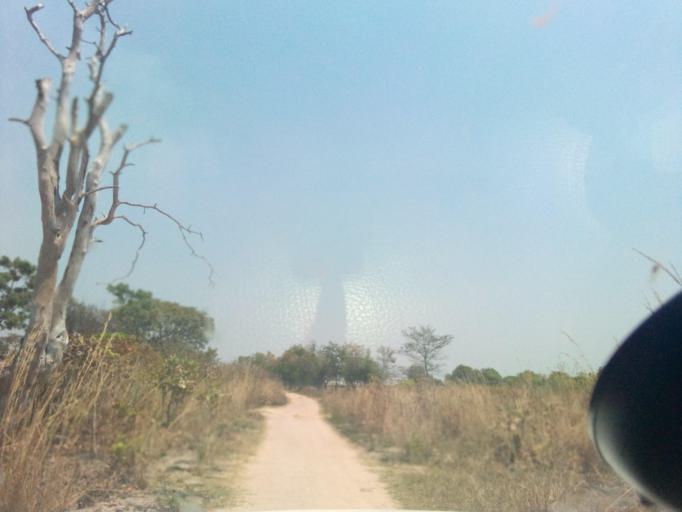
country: ZM
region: Copperbelt
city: Kataba
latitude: -12.2445
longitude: 30.3285
